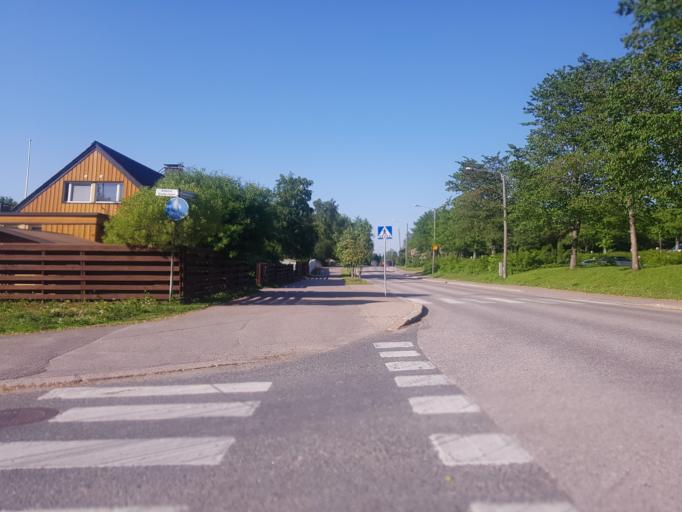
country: FI
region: Uusimaa
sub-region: Helsinki
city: Vantaa
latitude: 60.2641
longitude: 25.0128
